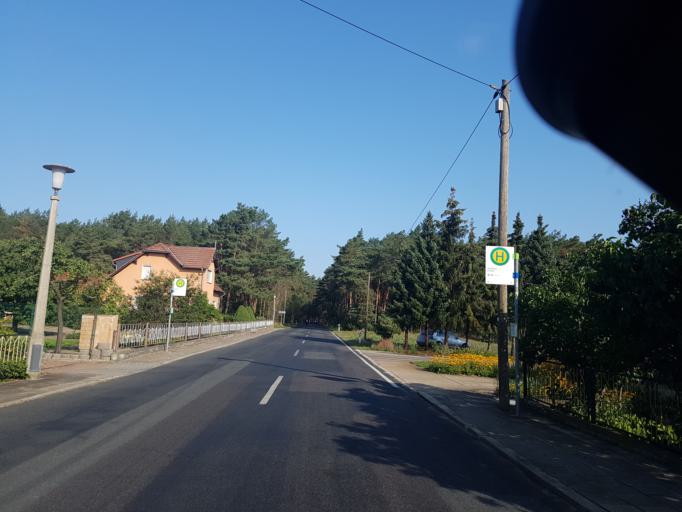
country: DE
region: Brandenburg
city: Niemegk
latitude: 52.1602
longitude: 12.6883
